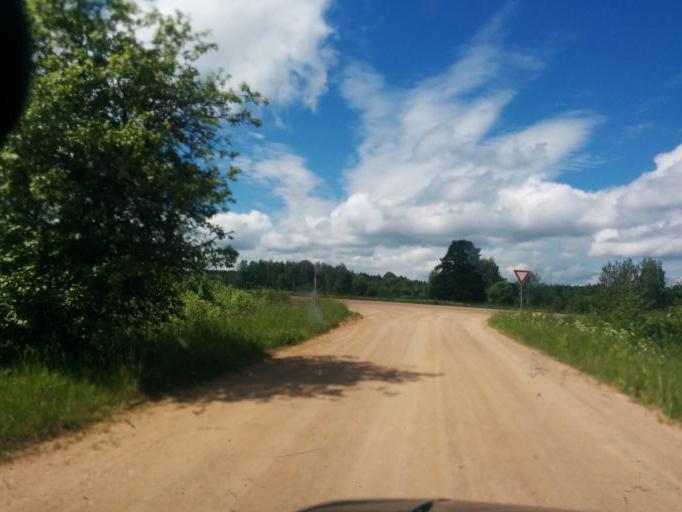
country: LV
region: Vilaka
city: Vilaka
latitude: 57.2754
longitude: 27.4773
